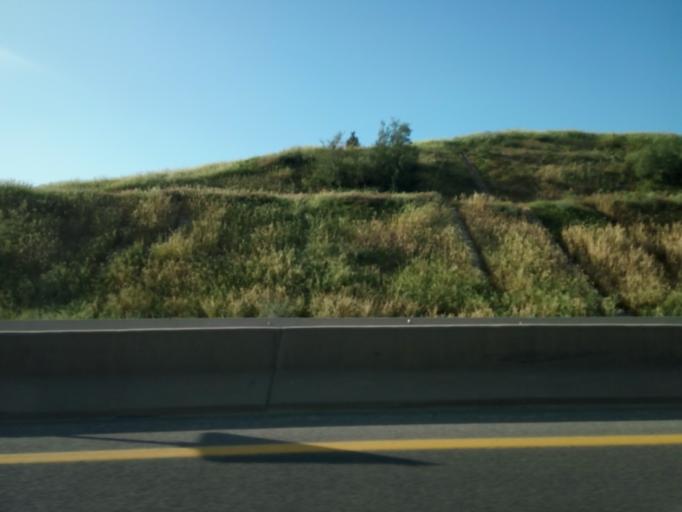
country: DZ
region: Boumerdes
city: Arbatache
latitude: 36.6456
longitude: 3.3630
